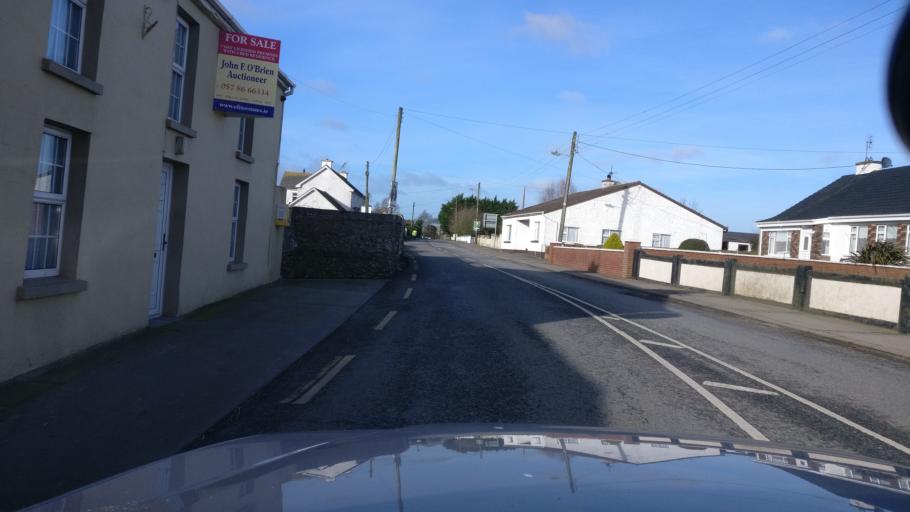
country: IE
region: Leinster
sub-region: Kilkenny
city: Castlecomer
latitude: 52.8604
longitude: -7.1631
